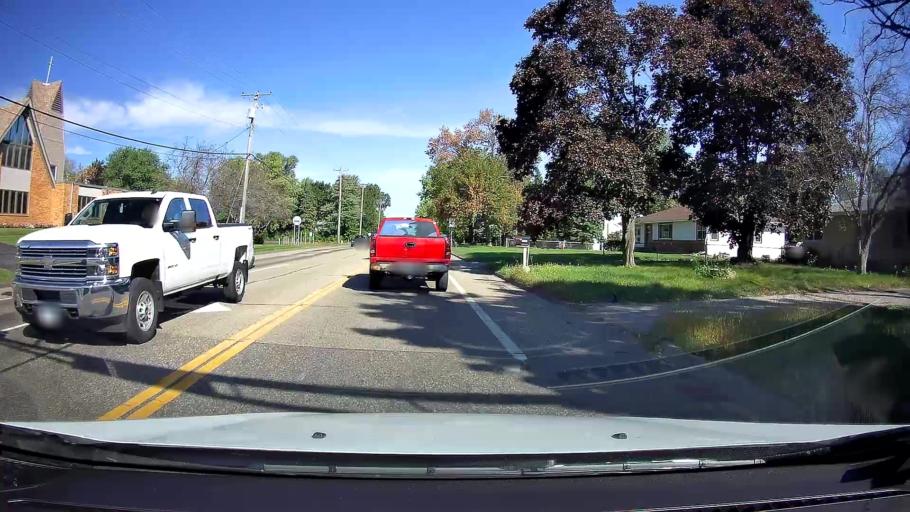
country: US
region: Minnesota
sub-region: Ramsey County
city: Roseville
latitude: 45.0209
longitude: -93.1570
